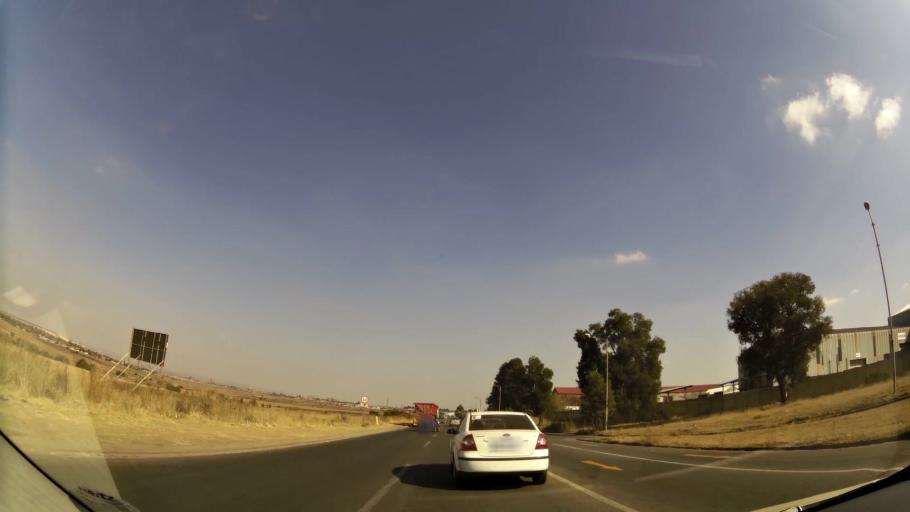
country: ZA
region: Gauteng
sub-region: City of Johannesburg Metropolitan Municipality
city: Roodepoort
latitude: -26.1479
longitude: 27.8130
